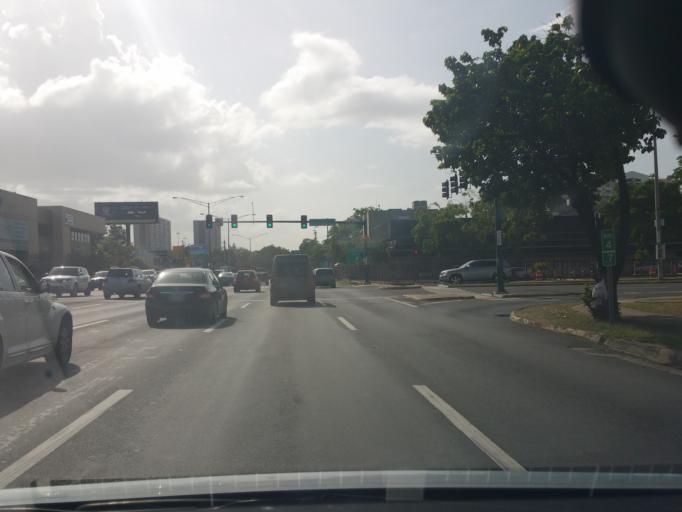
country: PR
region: Catano
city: Catano
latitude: 18.4077
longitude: -66.0647
